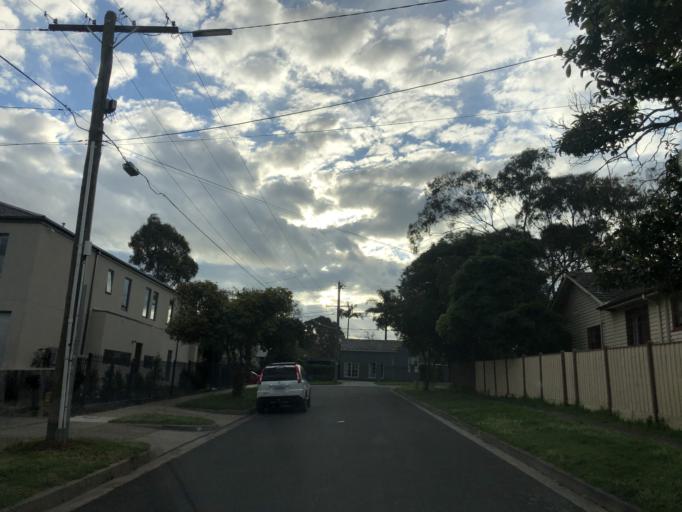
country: AU
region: Victoria
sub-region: Whitehorse
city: Burwood
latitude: -37.8642
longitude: 145.1249
